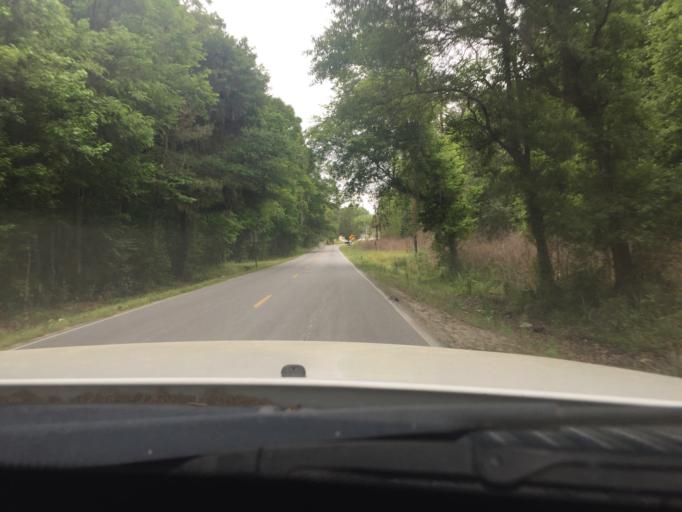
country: US
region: Georgia
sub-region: Chatham County
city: Georgetown
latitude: 31.9796
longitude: -81.2527
